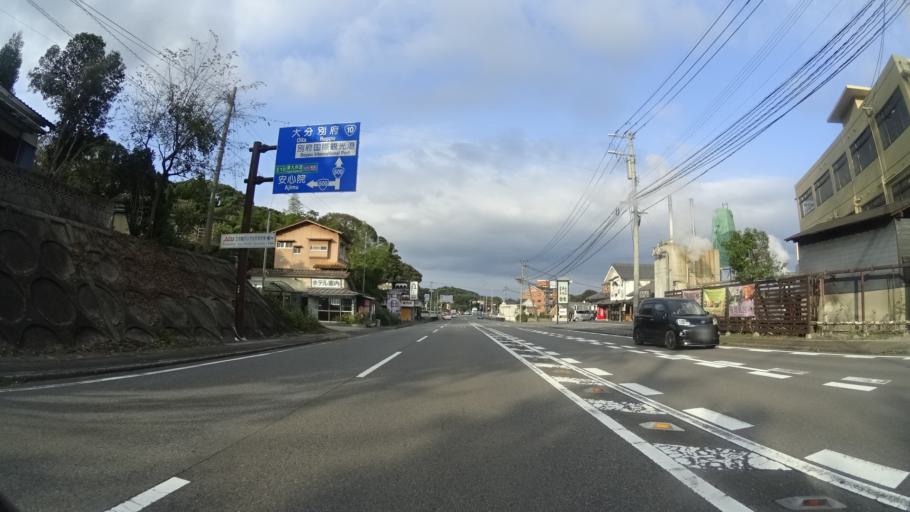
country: JP
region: Oita
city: Beppu
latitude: 33.3085
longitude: 131.4631
